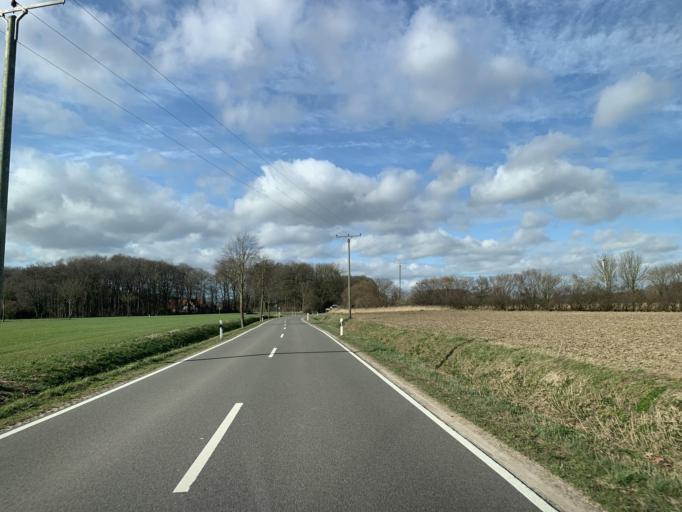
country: DE
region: North Rhine-Westphalia
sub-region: Regierungsbezirk Munster
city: Laer
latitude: 52.0211
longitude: 7.3408
